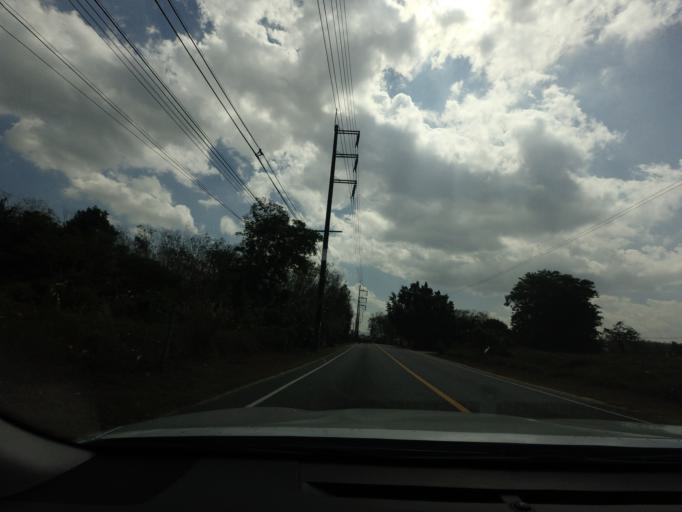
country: TH
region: Phangnga
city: Thai Mueang
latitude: 8.3900
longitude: 98.2681
